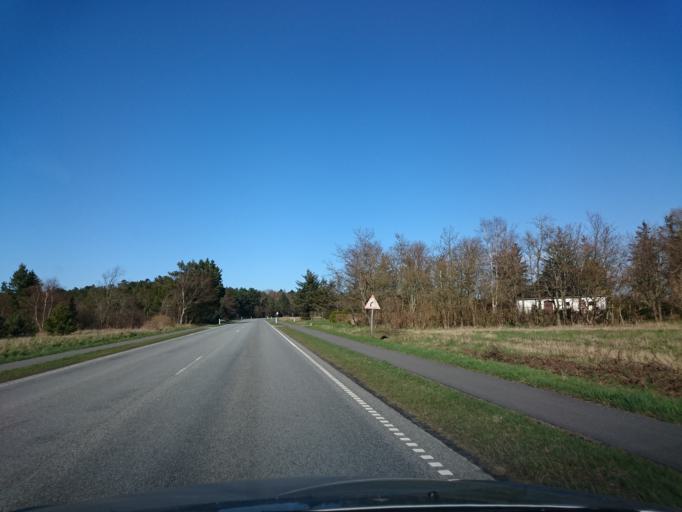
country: DK
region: North Denmark
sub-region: Hjorring Kommune
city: Sindal
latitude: 57.5847
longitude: 10.2250
